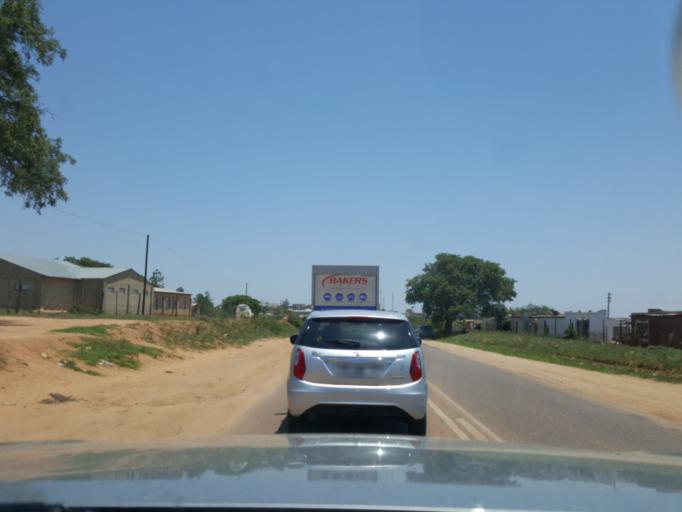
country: ZA
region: Limpopo
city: Thulamahashi
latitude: -24.6184
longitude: 31.0393
